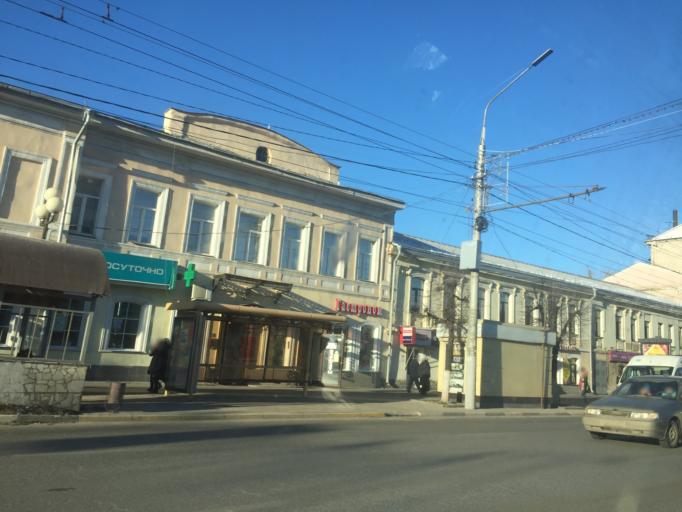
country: RU
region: Tula
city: Tula
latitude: 54.1892
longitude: 37.6132
